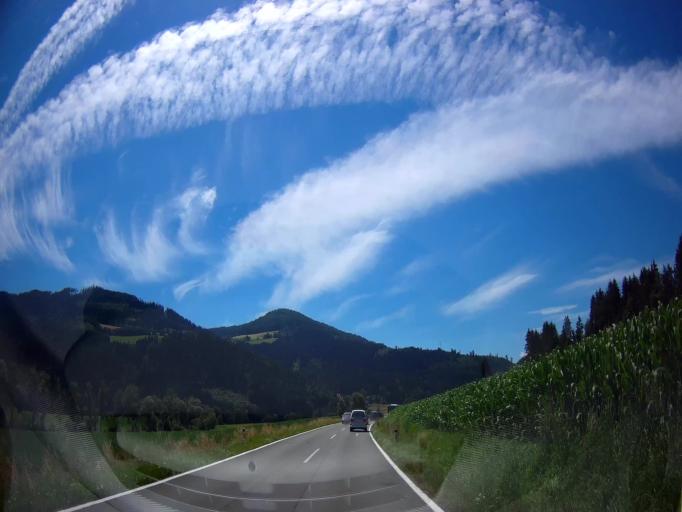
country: AT
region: Carinthia
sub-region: Politischer Bezirk Sankt Veit an der Glan
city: Strassburg
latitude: 46.8959
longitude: 14.3493
